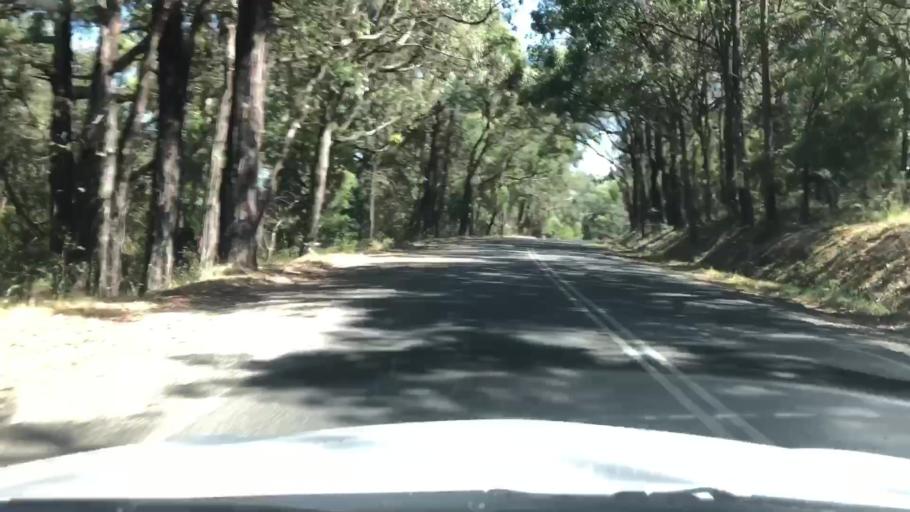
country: AU
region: Victoria
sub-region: Yarra Ranges
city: Macclesfield
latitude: -37.8781
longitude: 145.4777
